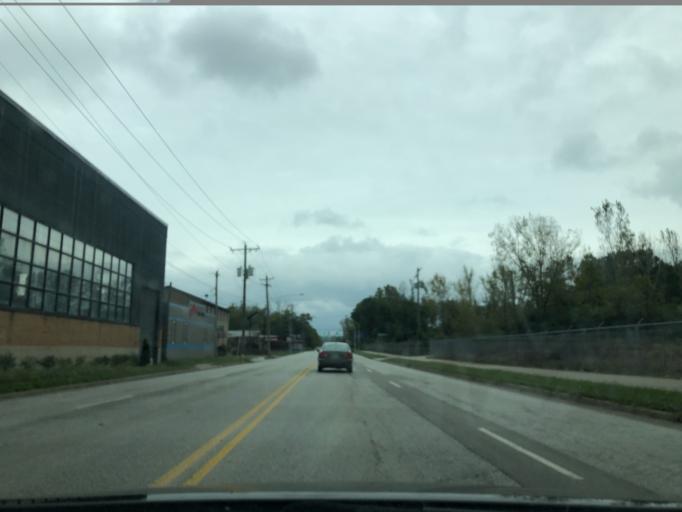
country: US
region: Kentucky
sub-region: Campbell County
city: Fort Thomas
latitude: 39.1084
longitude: -84.4369
